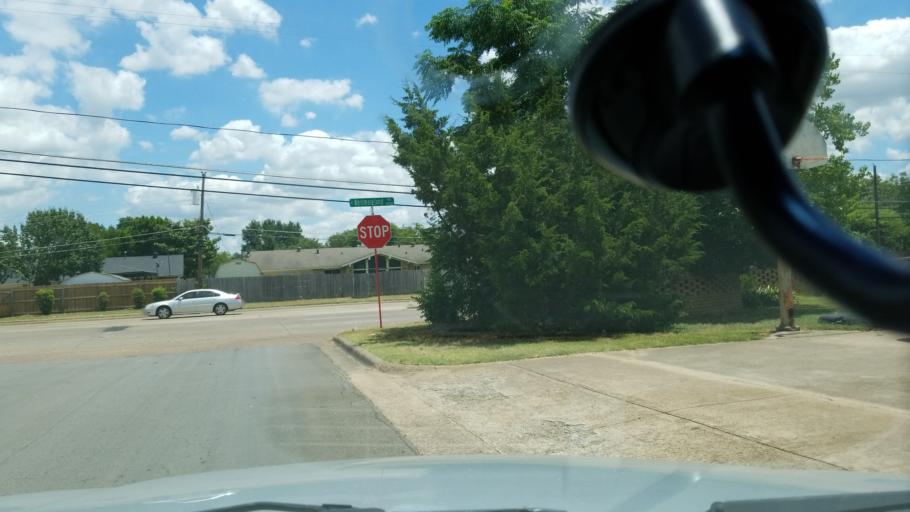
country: US
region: Texas
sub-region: Dallas County
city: Cockrell Hill
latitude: 32.6956
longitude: -96.8791
